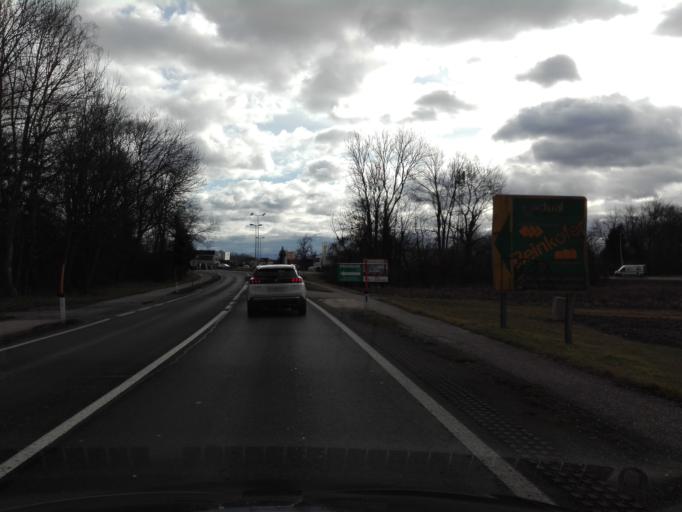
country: AT
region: Upper Austria
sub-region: Politischer Bezirk Linz-Land
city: Traun
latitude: 48.2103
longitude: 14.2435
